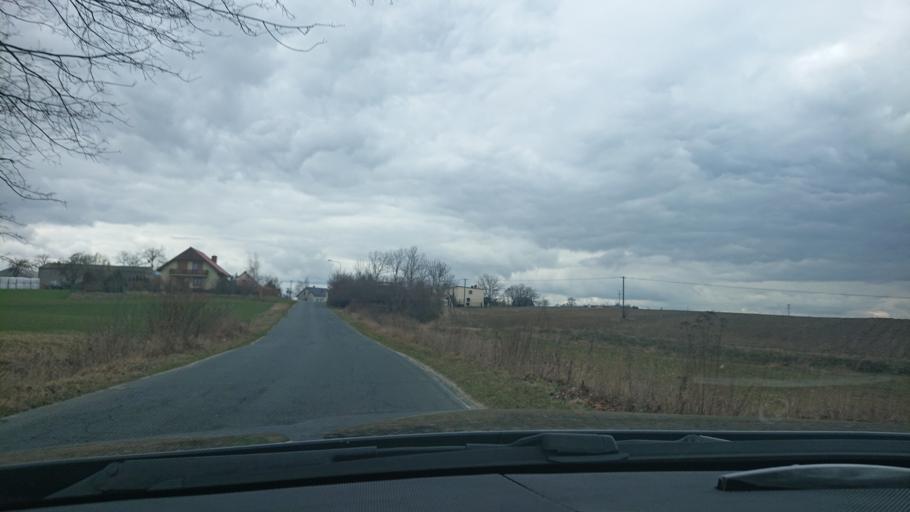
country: PL
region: Greater Poland Voivodeship
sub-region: Powiat gnieznienski
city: Gniezno
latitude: 52.5836
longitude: 17.6572
